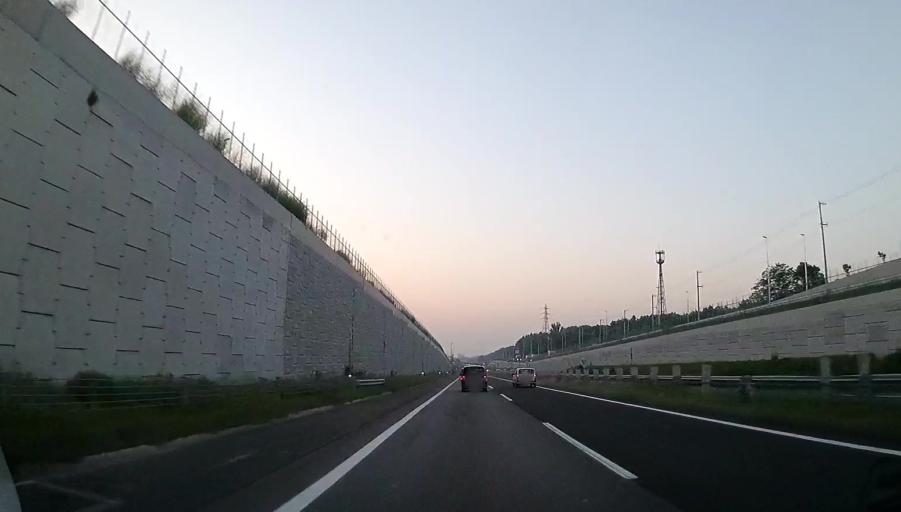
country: JP
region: Hokkaido
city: Kitahiroshima
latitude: 42.9936
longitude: 141.4690
